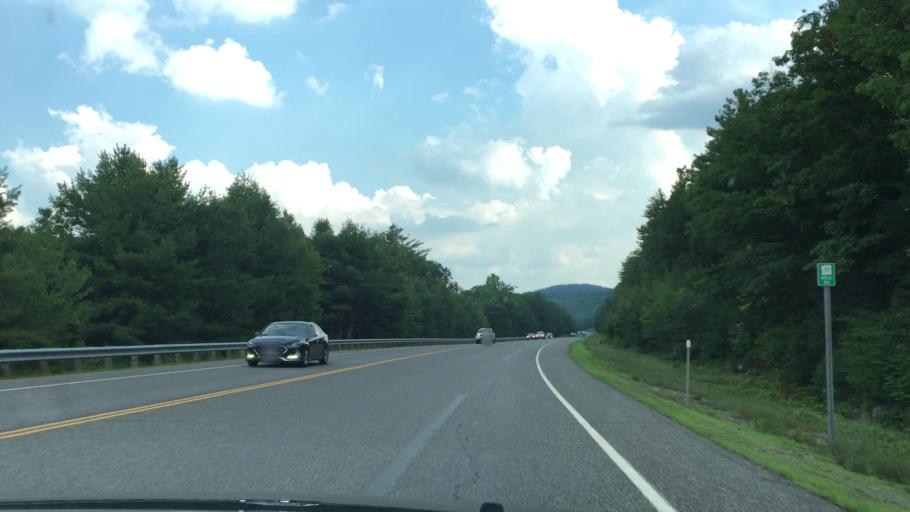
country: US
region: New Hampshire
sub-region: Carroll County
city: Wolfeboro
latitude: 43.5310
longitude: -71.2750
